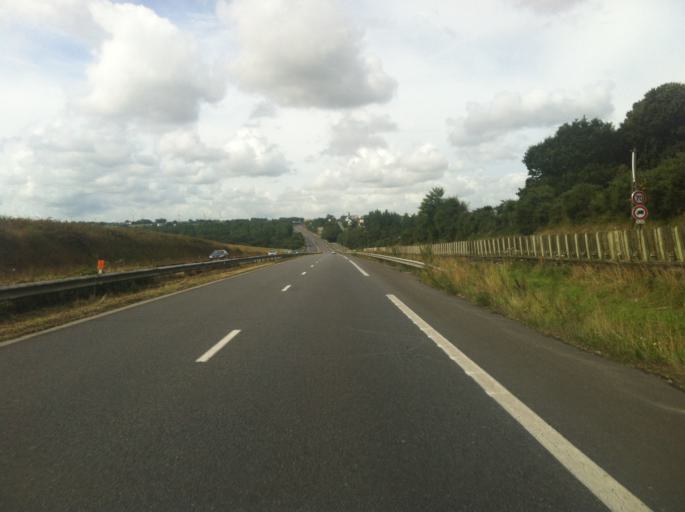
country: FR
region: Brittany
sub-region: Departement du Finistere
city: Morlaix
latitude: 48.5645
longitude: -3.8611
